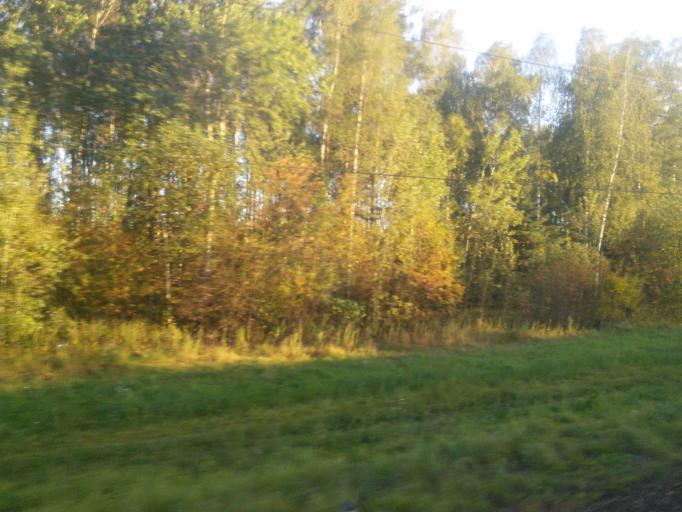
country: RU
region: Moskovskaya
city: Fryazevo
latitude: 55.7474
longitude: 38.5327
